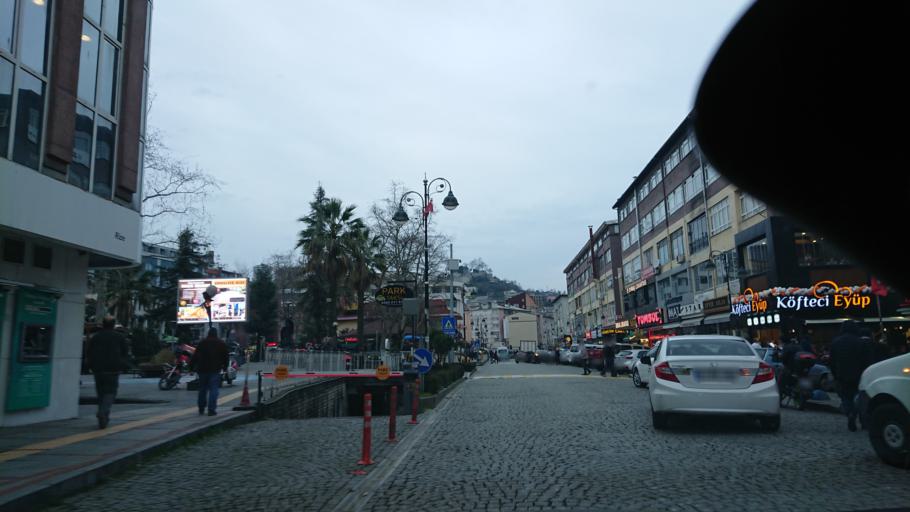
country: TR
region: Rize
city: Rize
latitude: 41.0251
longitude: 40.5192
